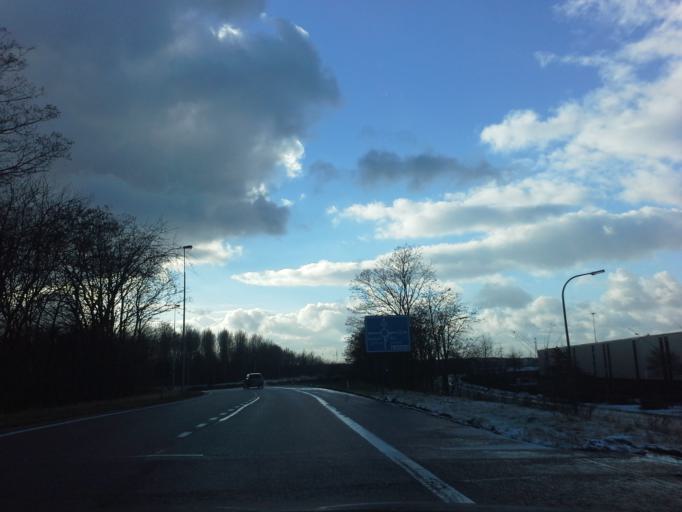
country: BE
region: Flanders
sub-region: Provincie Limburg
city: Overpelt
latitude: 51.2200
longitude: 5.3991
